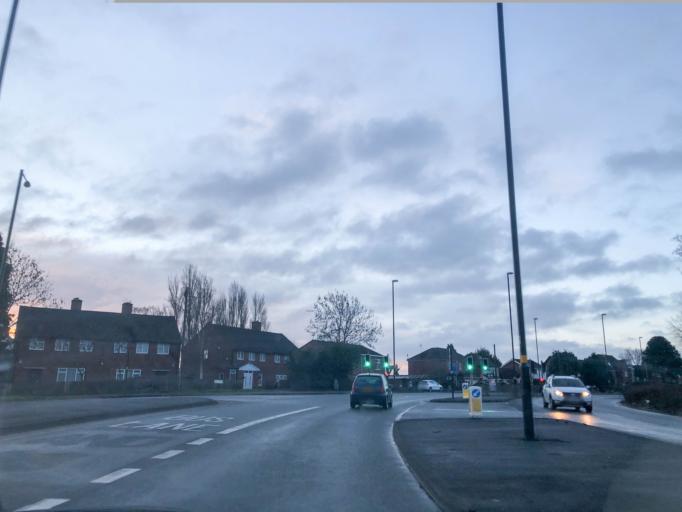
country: GB
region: England
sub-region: Solihull
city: Tidbury Green
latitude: 52.4139
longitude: -1.8847
